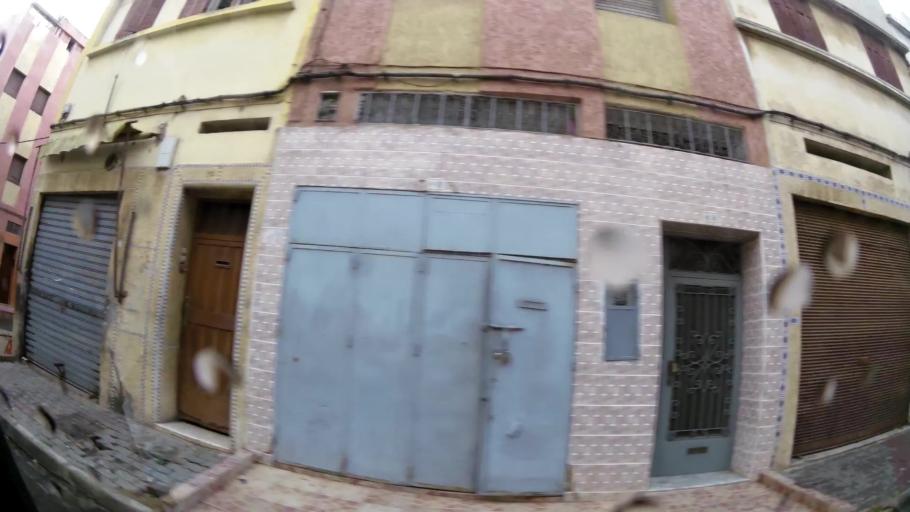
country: MA
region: Grand Casablanca
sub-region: Casablanca
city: Casablanca
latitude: 33.5510
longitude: -7.5834
